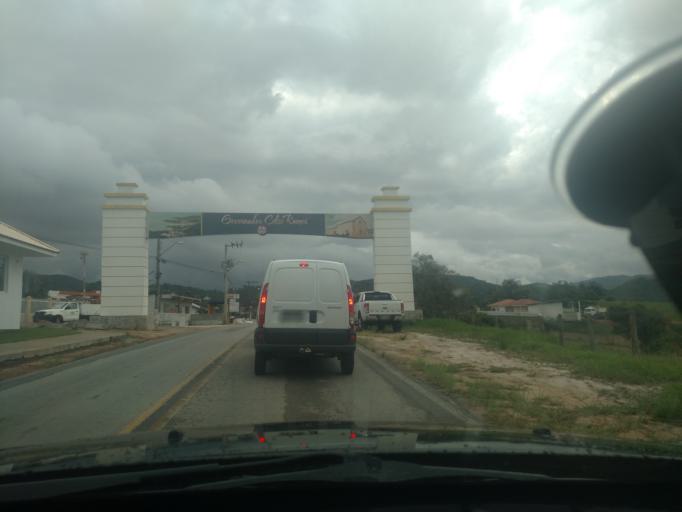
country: BR
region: Santa Catarina
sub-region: Biguacu
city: Biguacu
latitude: -27.3781
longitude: -48.6259
